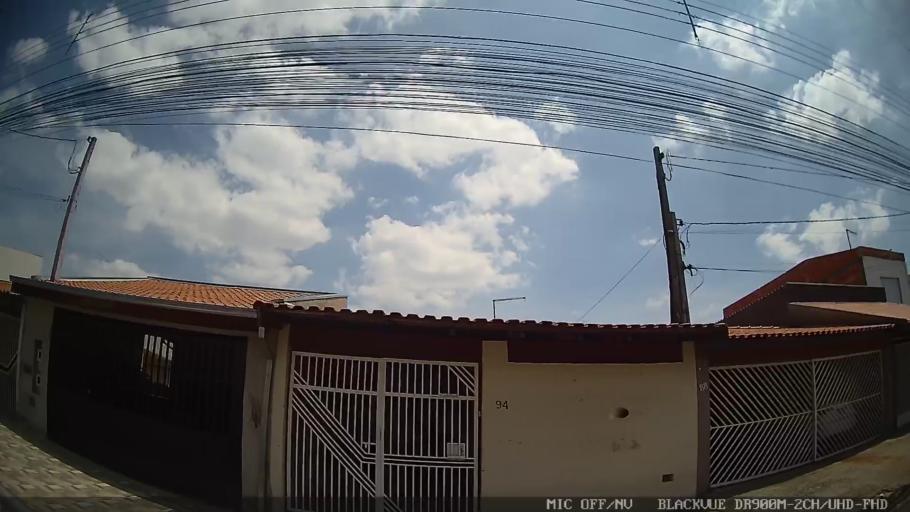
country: BR
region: Sao Paulo
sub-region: Cabreuva
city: Cabreuva
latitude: -23.2579
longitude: -47.0525
